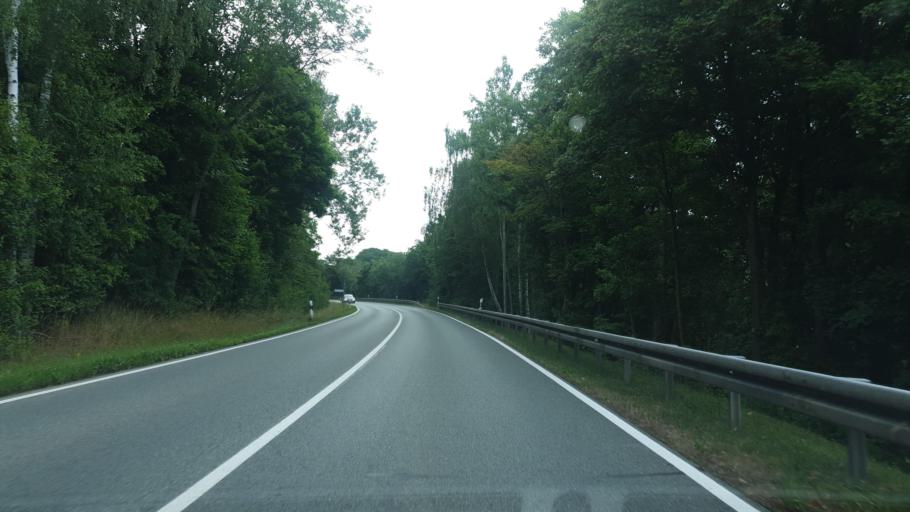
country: DE
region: Saxony
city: Pohl
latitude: 50.5552
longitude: 12.1911
